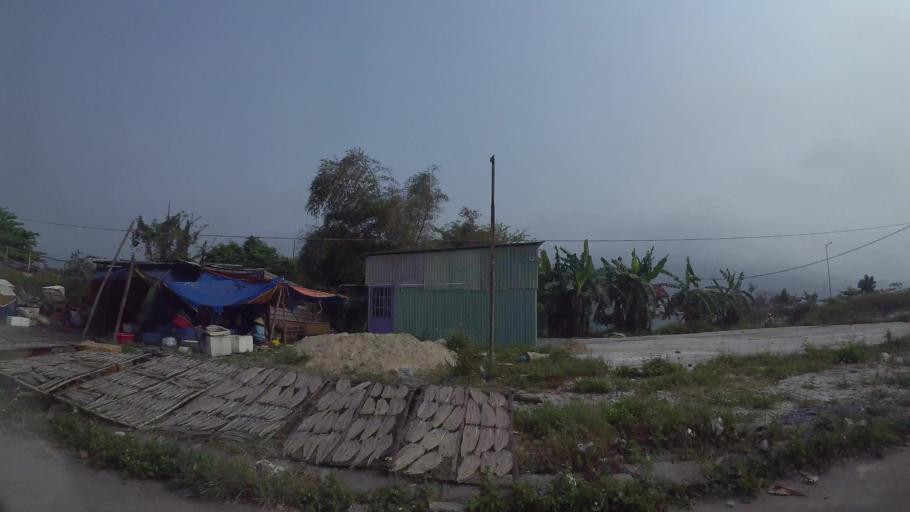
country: VN
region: Da Nang
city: Son Tra
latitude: 16.0964
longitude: 108.2519
